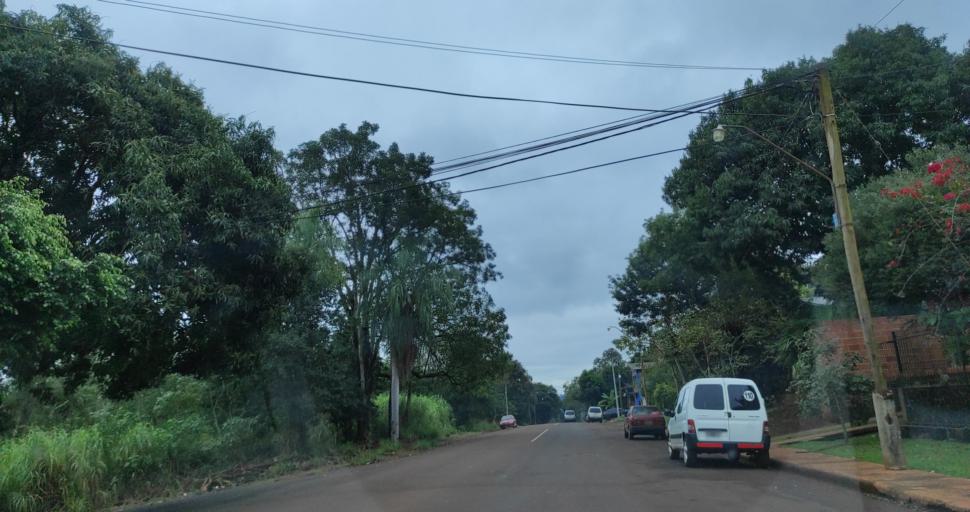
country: AR
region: Misiones
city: Puerto Rico
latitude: -26.8005
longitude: -55.0204
